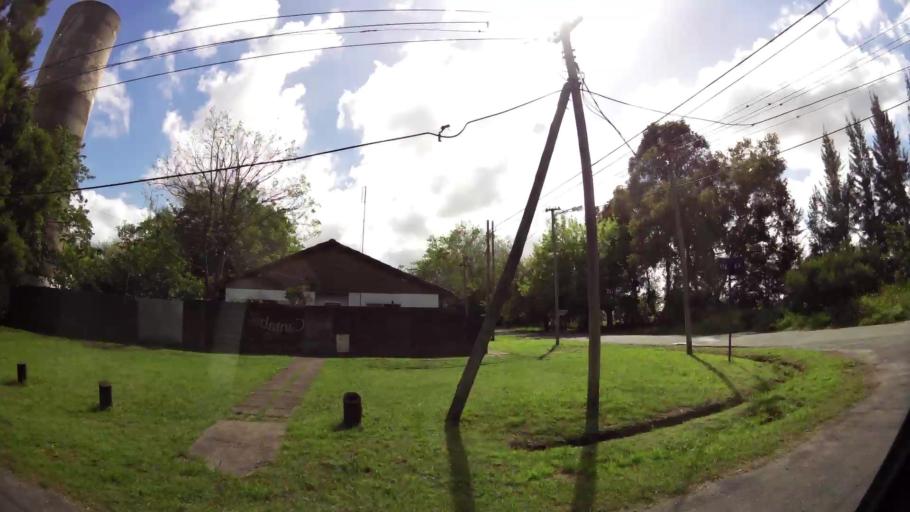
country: AR
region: Buenos Aires
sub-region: Partido de Quilmes
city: Quilmes
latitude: -34.7973
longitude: -58.1555
